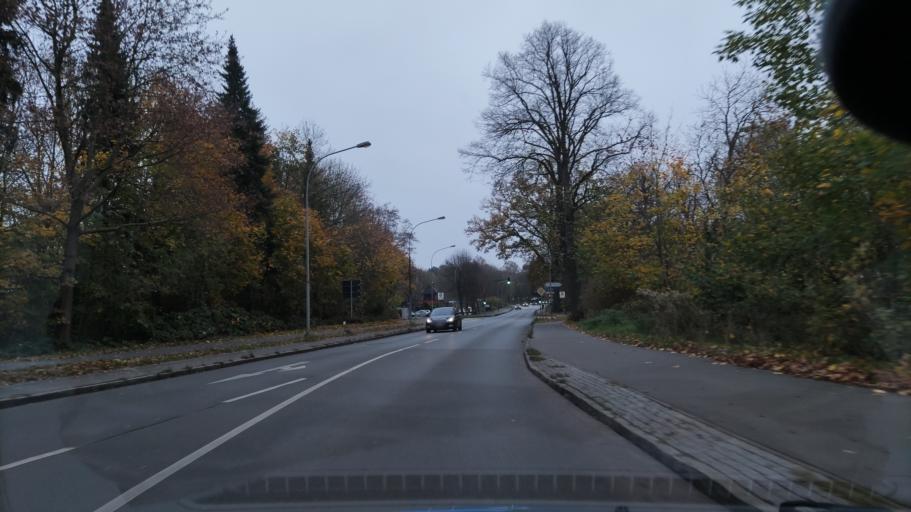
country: DE
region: Schleswig-Holstein
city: Luebeck
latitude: 53.8351
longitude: 10.7140
